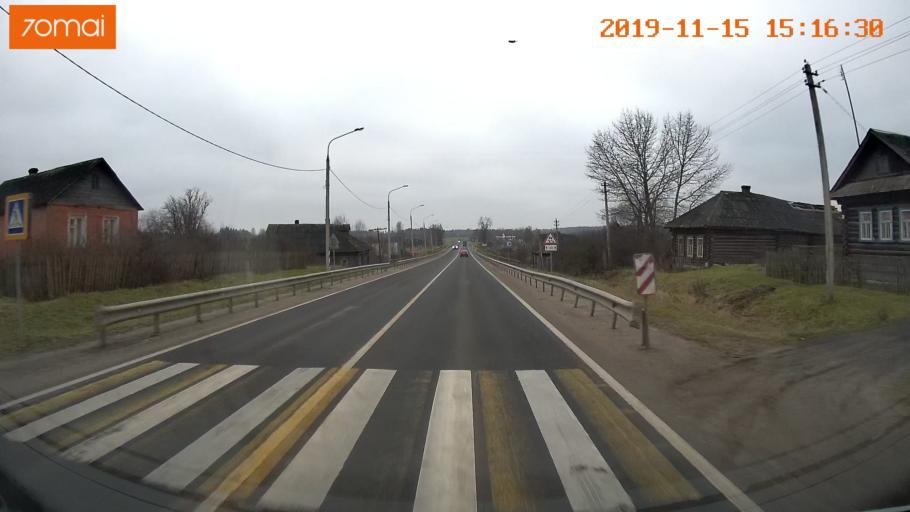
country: RU
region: Jaroslavl
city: Danilov
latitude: 58.2725
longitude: 40.1906
